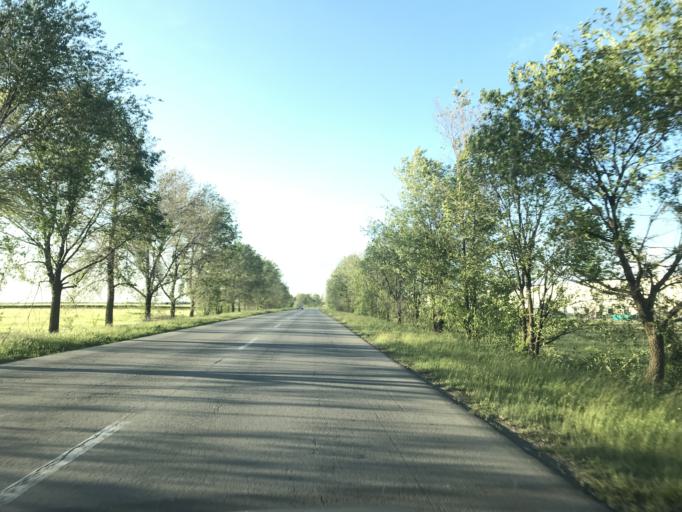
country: RS
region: Autonomna Pokrajina Vojvodina
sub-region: Srednjebanatski Okrug
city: Zrenjanin
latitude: 45.3861
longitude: 20.3520
